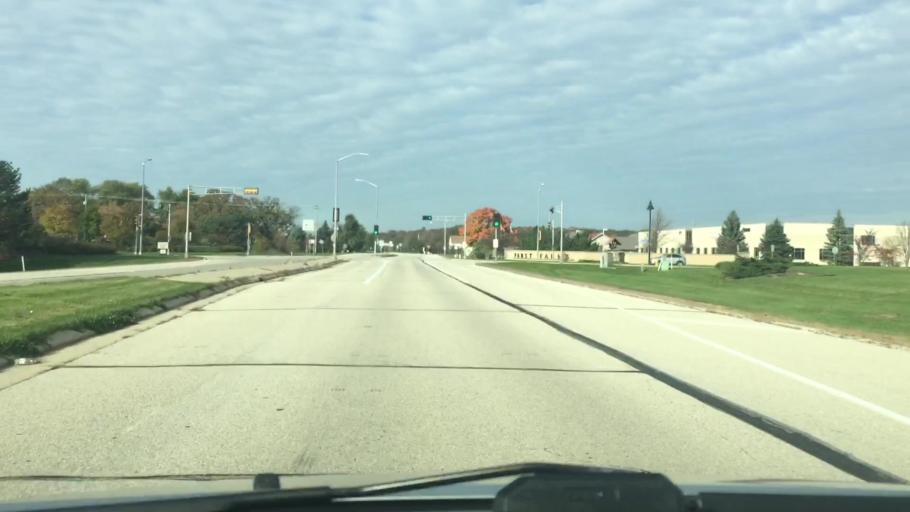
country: US
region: Wisconsin
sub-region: Waukesha County
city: Dousman
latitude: 43.0622
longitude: -88.4781
